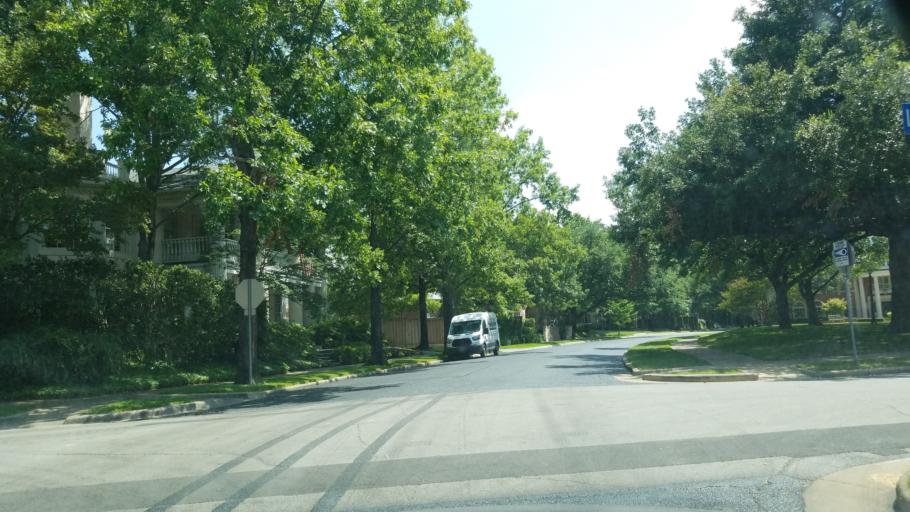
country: US
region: Texas
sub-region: Dallas County
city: Highland Park
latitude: 32.8282
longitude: -96.7911
